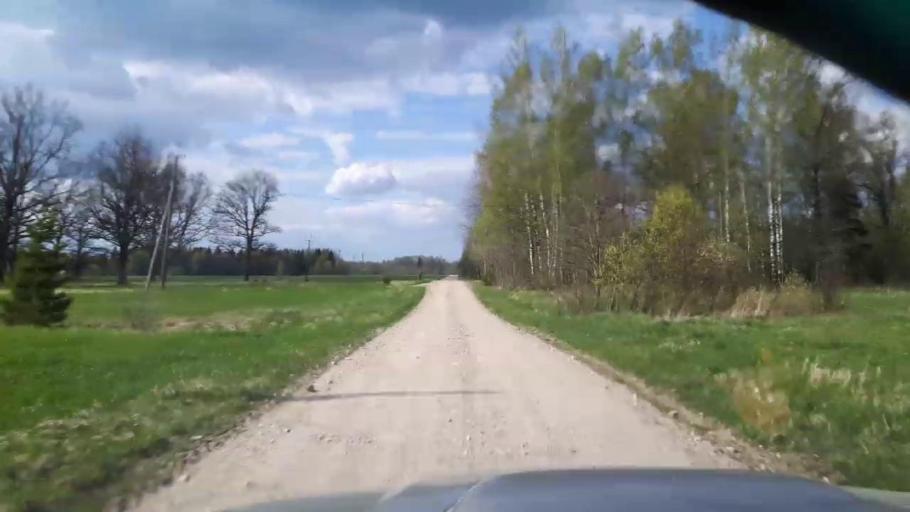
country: EE
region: Paernumaa
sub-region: Sindi linn
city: Sindi
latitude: 58.4404
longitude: 24.7588
